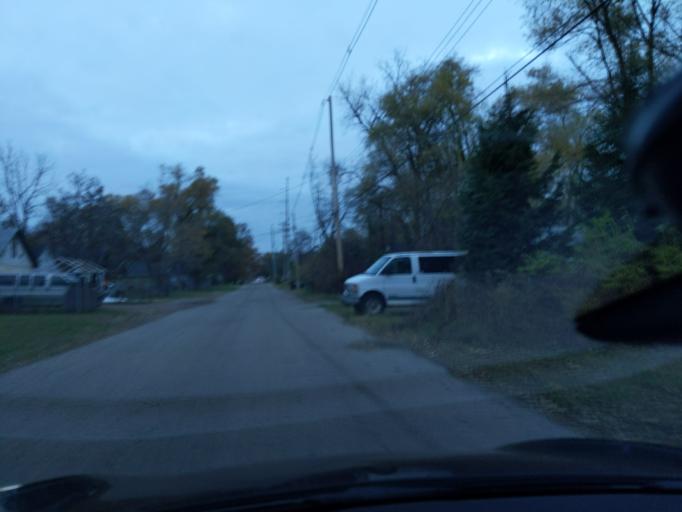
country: US
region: Michigan
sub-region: Ingham County
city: East Lansing
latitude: 42.7275
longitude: -84.5125
